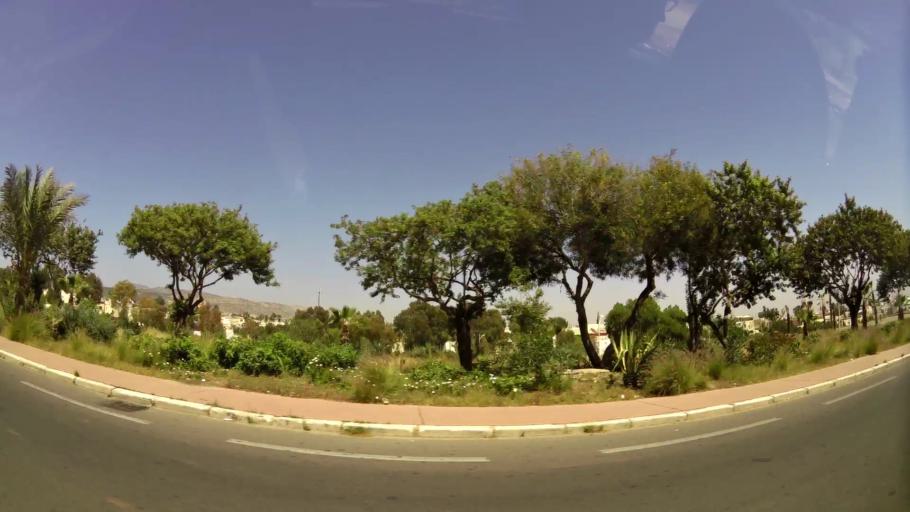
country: MA
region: Souss-Massa-Draa
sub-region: Agadir-Ida-ou-Tnan
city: Agadir
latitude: 30.4322
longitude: -9.5941
